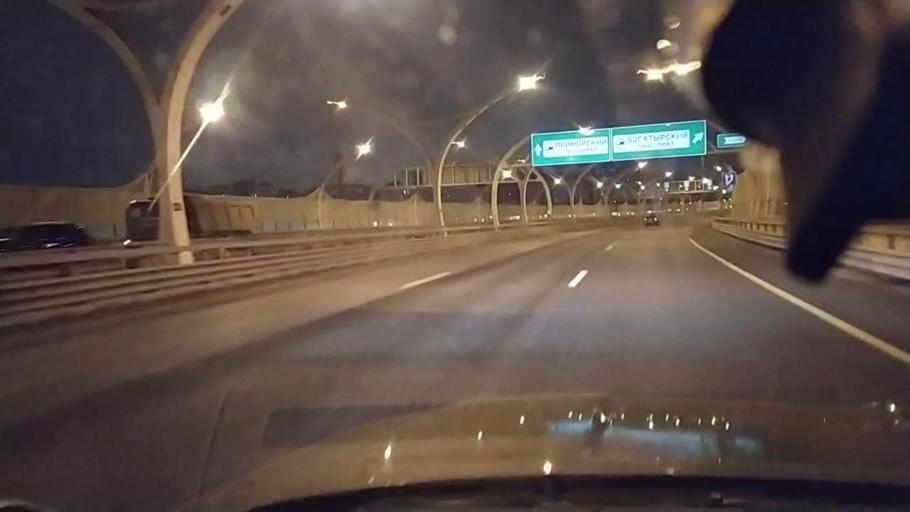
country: RU
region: St.-Petersburg
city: Staraya Derevnya
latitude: 60.0096
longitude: 30.2331
